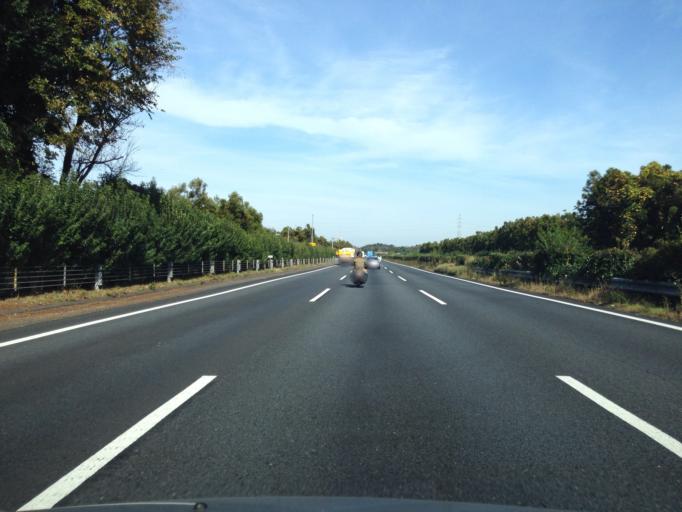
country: JP
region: Ibaraki
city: Ishioka
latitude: 36.1826
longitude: 140.2513
